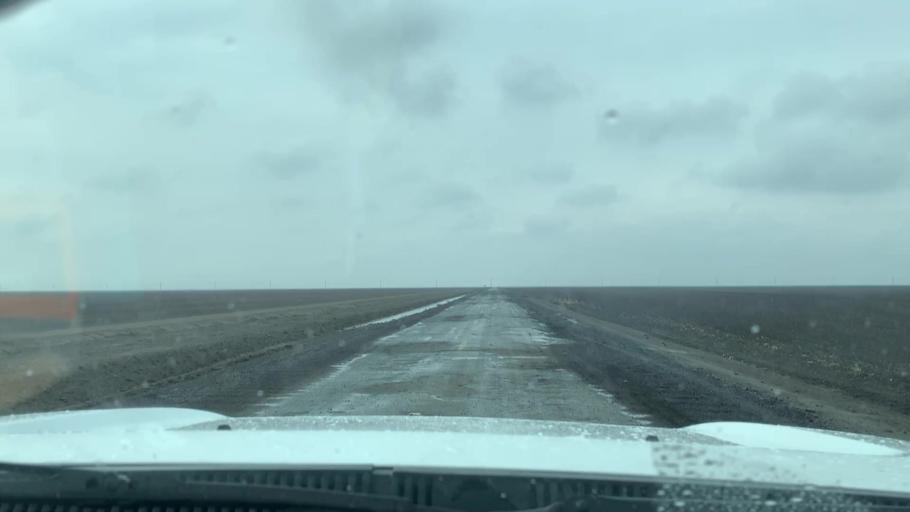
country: US
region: California
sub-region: Kings County
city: Corcoran
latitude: 36.0072
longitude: -119.5563
